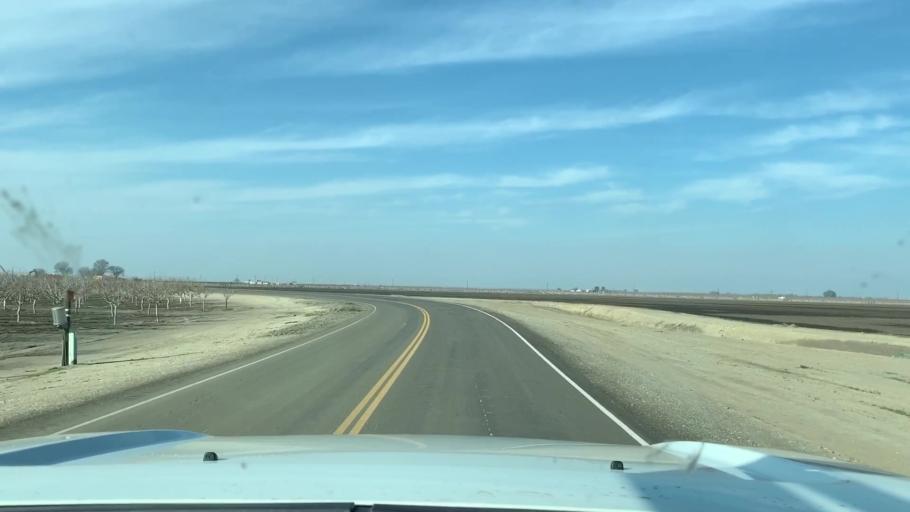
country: US
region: California
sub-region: Kern County
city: Buttonwillow
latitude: 35.4519
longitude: -119.5613
